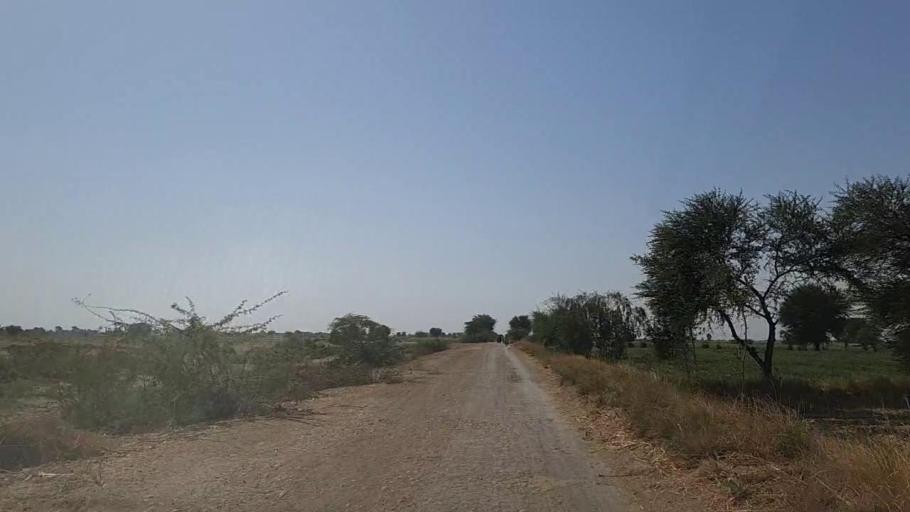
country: PK
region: Sindh
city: Samaro
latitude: 25.2287
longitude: 69.4073
